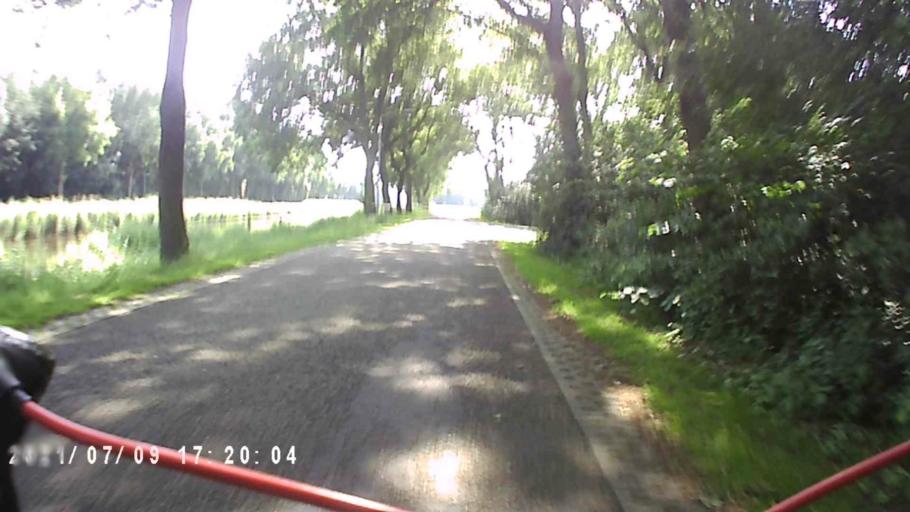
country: NL
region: Groningen
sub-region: Gemeente Vlagtwedde
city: Vlagtwedde
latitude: 53.0872
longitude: 7.1658
